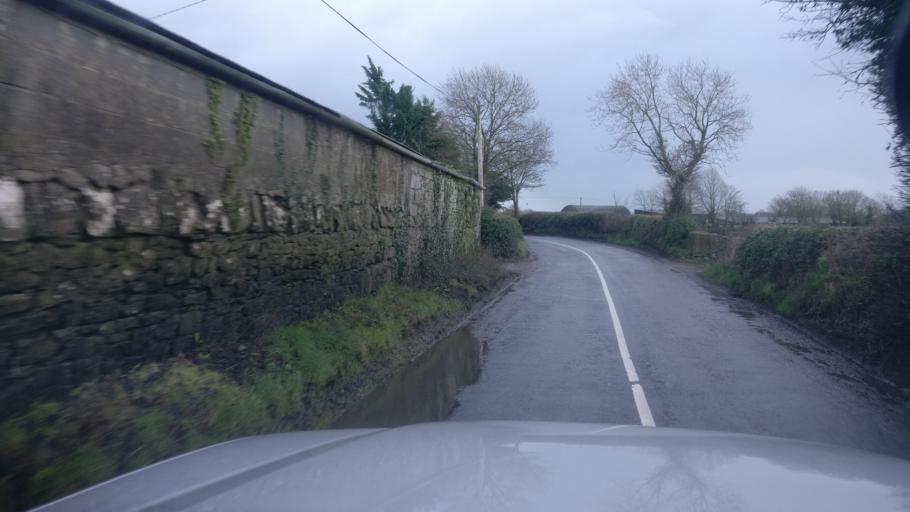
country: IE
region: Munster
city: Nenagh Bridge
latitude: 52.9794
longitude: -8.0949
